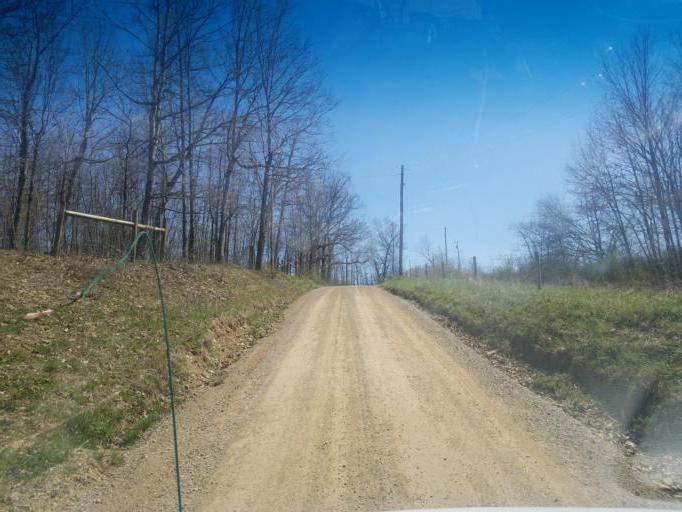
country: US
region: Ohio
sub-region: Knox County
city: Oak Hill
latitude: 40.3688
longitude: -82.2236
